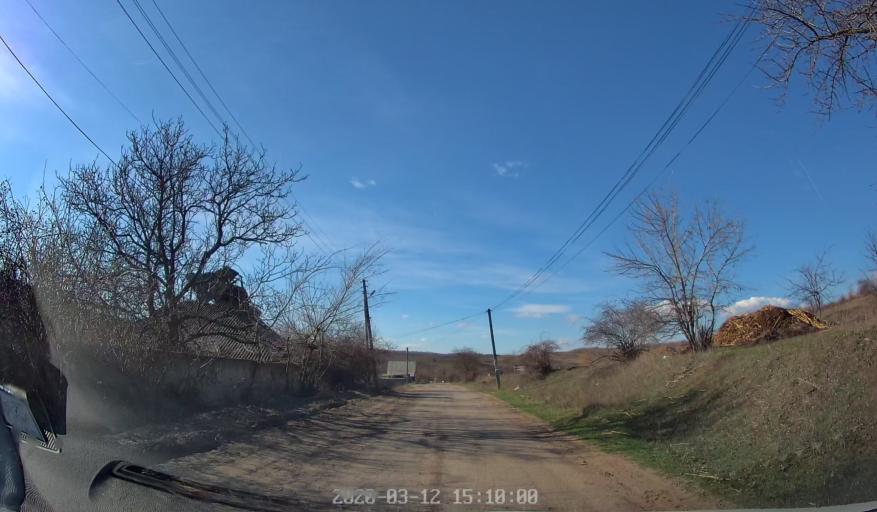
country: MD
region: Chisinau
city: Ciorescu
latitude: 47.2248
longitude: 28.9825
